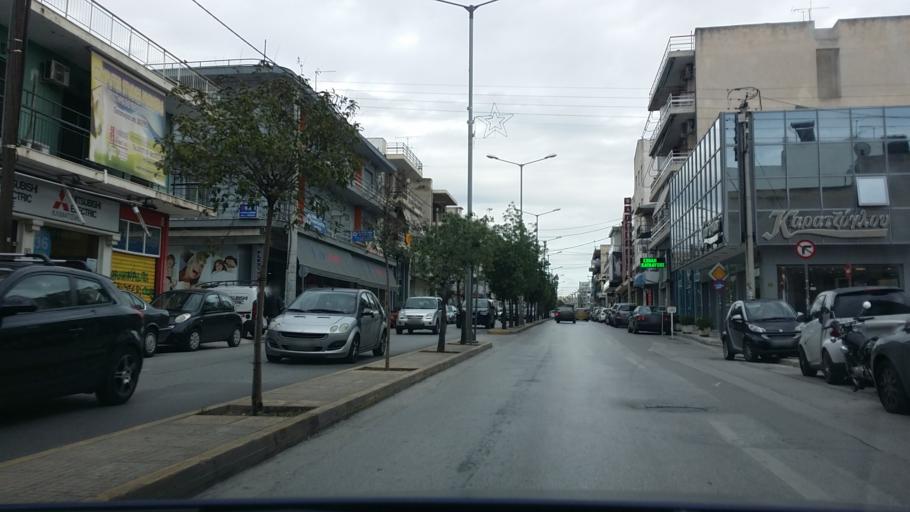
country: GR
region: Attica
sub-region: Nomarchia Athinas
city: Peristeri
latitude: 38.0147
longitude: 23.6904
